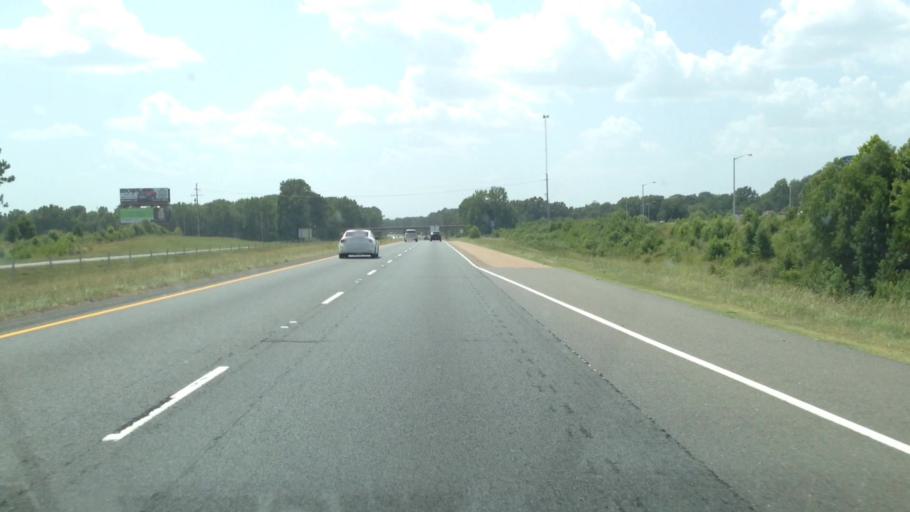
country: US
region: Louisiana
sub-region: Bienville Parish
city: Arcadia
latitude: 32.5648
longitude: -92.9157
